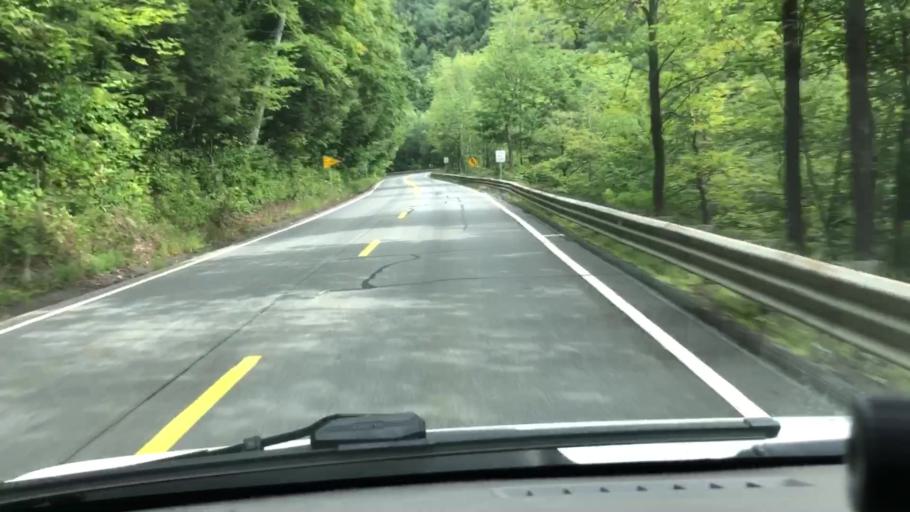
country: US
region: Massachusetts
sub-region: Franklin County
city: Charlemont
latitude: 42.6348
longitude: -72.9777
